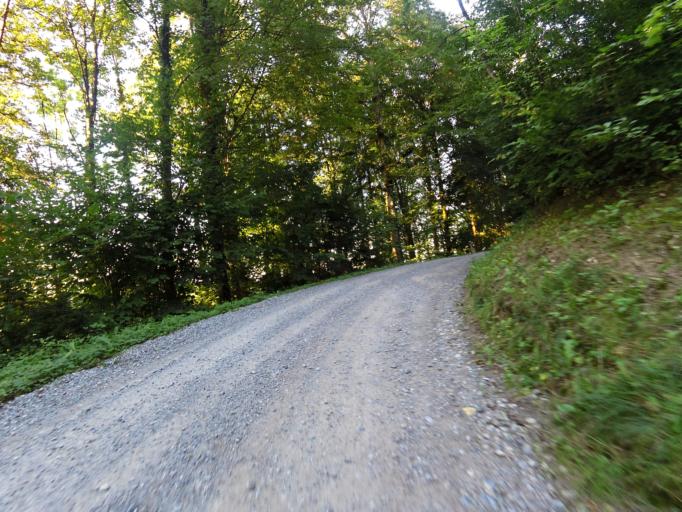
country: CH
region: Thurgau
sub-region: Weinfelden District
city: Wigoltingen
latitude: 47.5793
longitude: 9.0178
